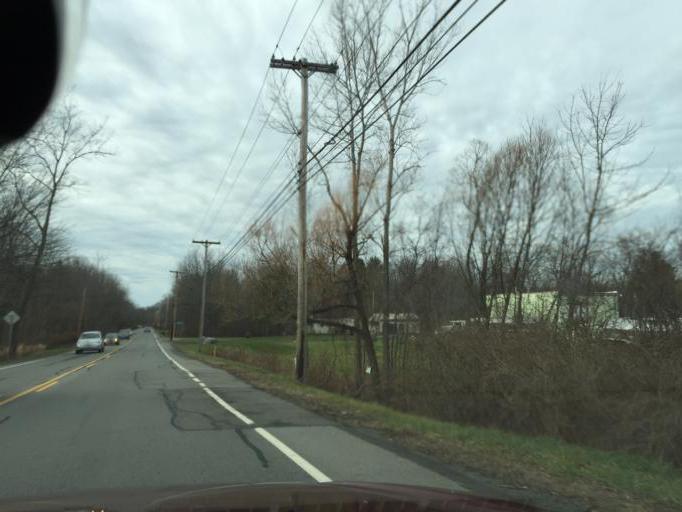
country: US
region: New York
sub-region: Monroe County
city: North Gates
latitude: 43.0935
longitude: -77.6915
